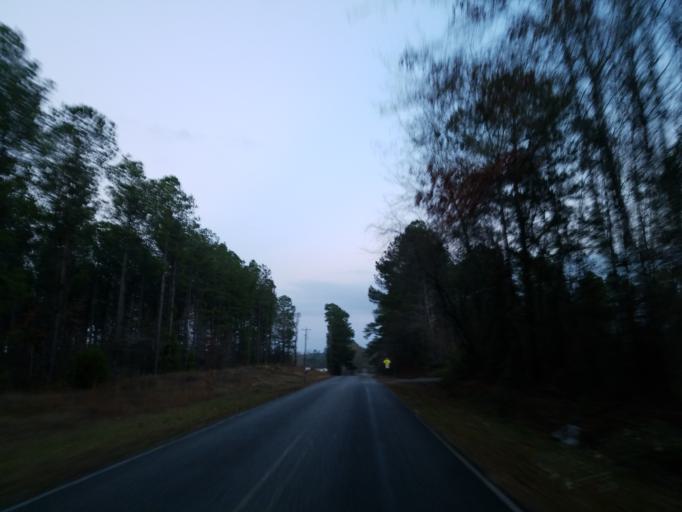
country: US
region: Alabama
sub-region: Sumter County
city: York
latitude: 32.4064
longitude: -88.4532
